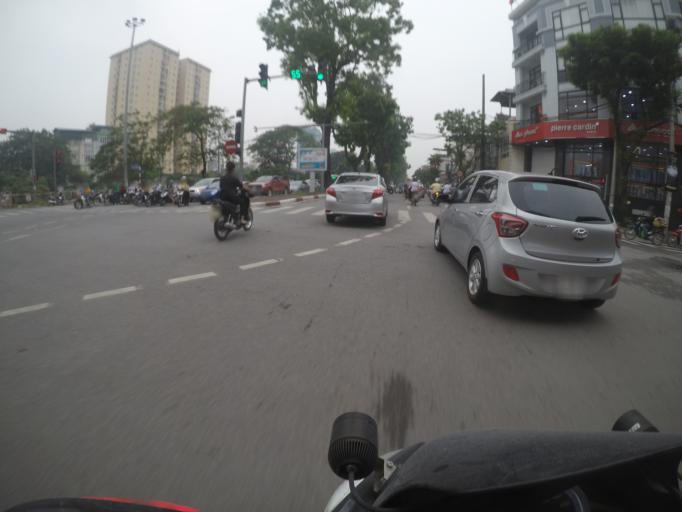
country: VN
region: Ha Noi
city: Thanh Xuan
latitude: 21.0109
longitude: 105.8111
